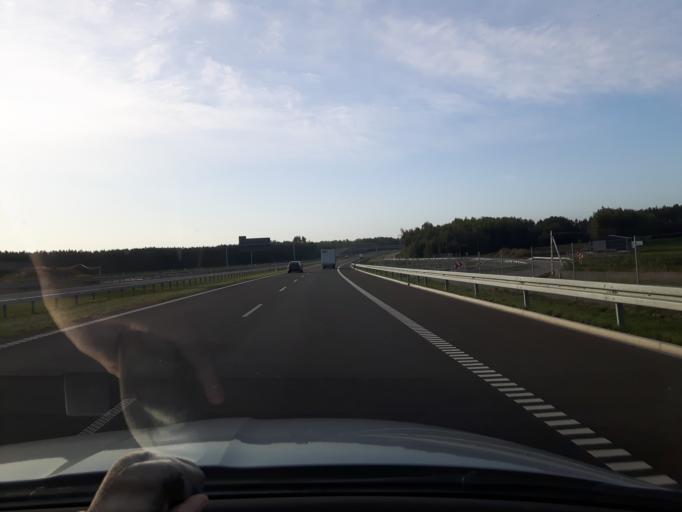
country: PL
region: Masovian Voivodeship
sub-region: Powiat radomski
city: Jedlinsk
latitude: 51.5271
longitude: 21.0833
